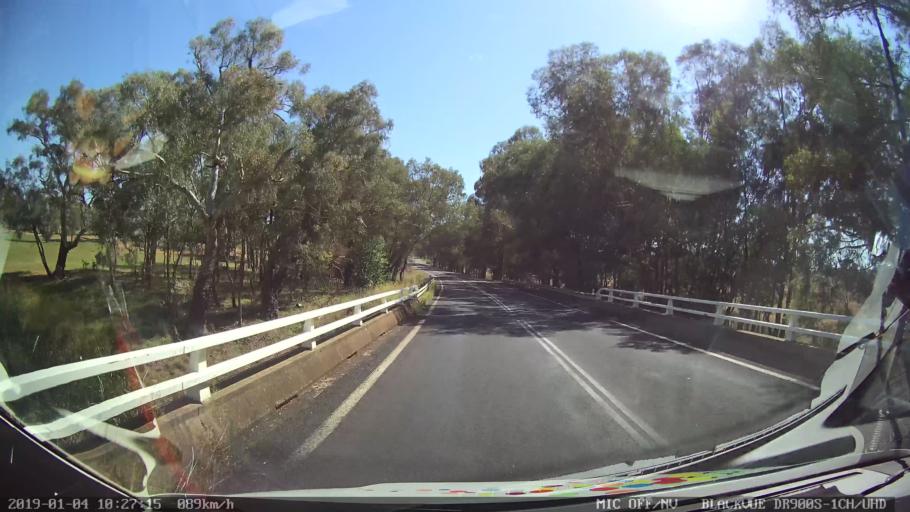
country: AU
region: New South Wales
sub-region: Cabonne
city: Canowindra
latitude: -33.3724
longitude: 148.5971
